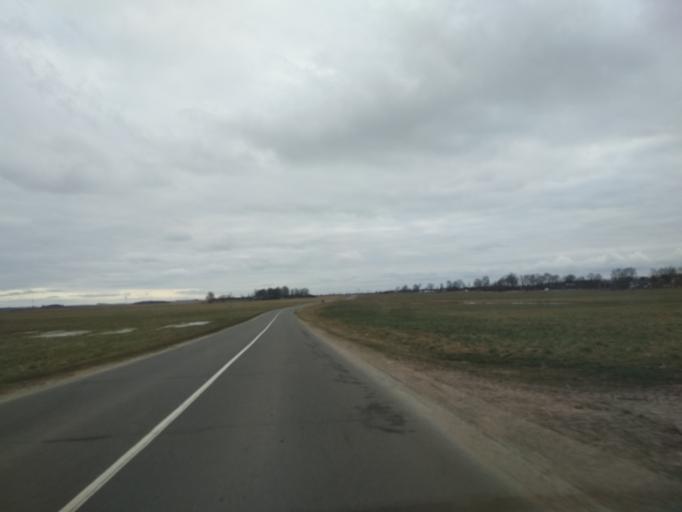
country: BY
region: Minsk
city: Svislach
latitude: 53.5673
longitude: 28.0169
